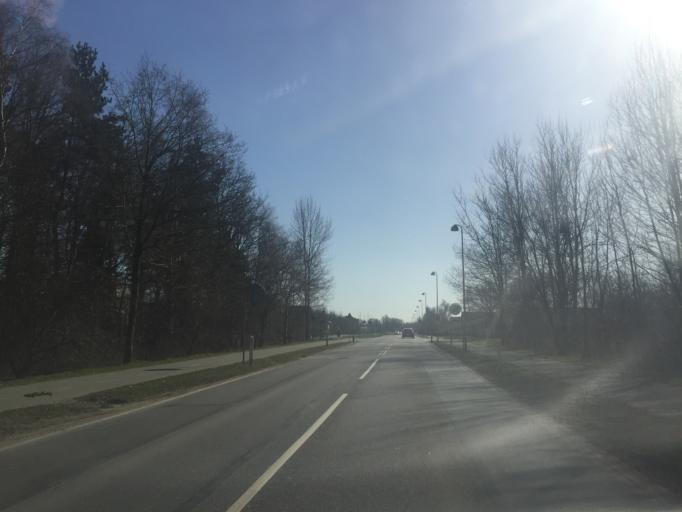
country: DK
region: Capital Region
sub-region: Glostrup Kommune
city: Glostrup
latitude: 55.6860
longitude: 12.4209
